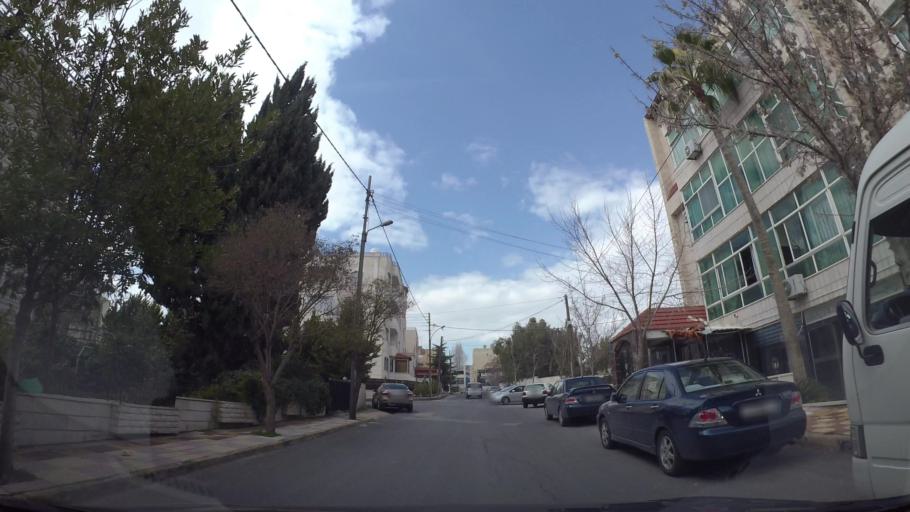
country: JO
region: Amman
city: Amman
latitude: 31.9717
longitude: 35.9022
